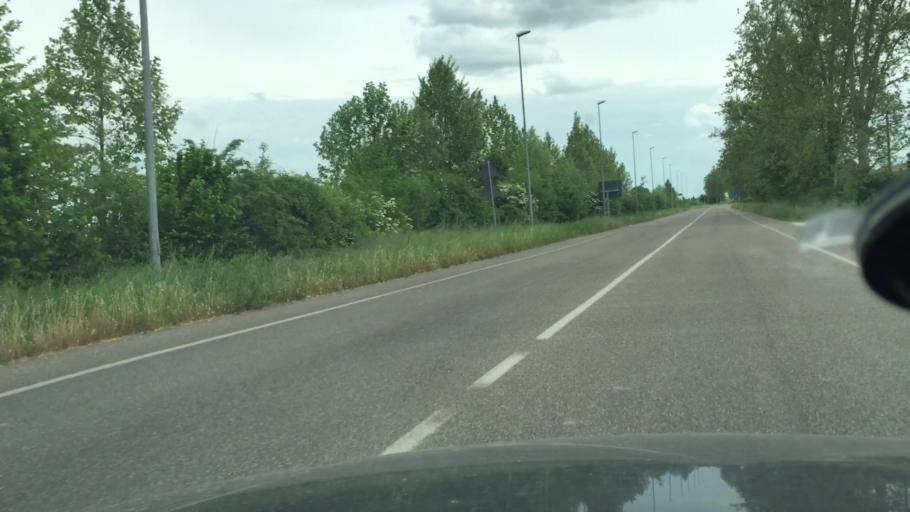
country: IT
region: Emilia-Romagna
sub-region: Provincia di Ferrara
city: Cona
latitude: 44.8005
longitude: 11.7165
